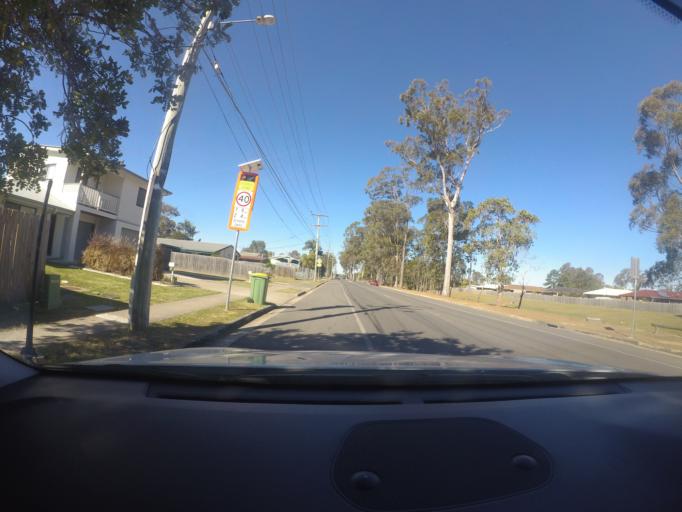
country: AU
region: Queensland
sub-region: Logan
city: Waterford West
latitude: -27.6866
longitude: 153.1315
